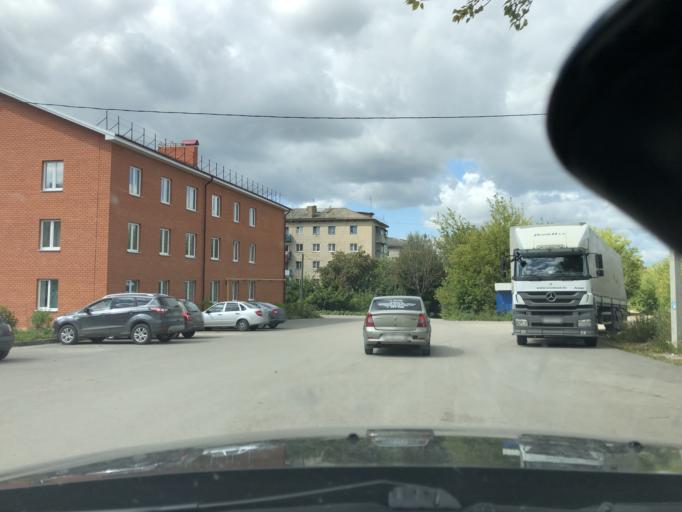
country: RU
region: Tula
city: Yasnogorsk
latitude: 54.4749
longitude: 37.6979
